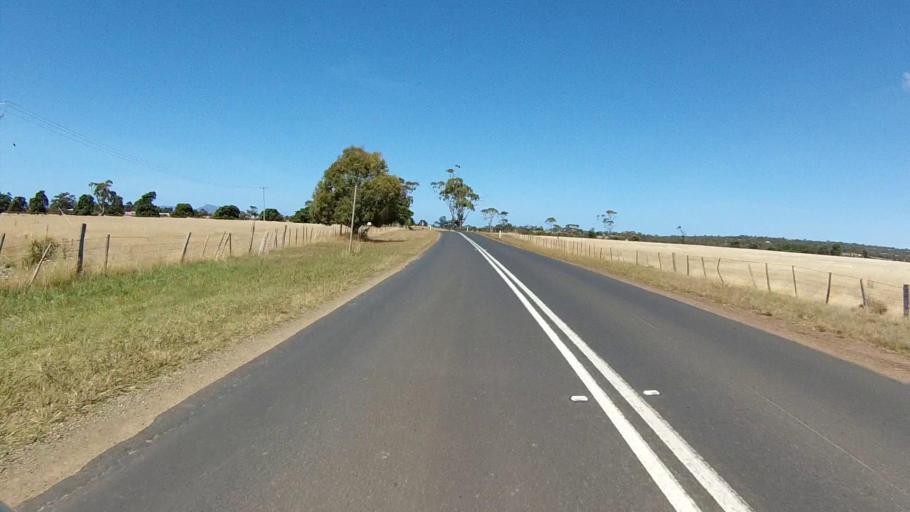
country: AU
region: Tasmania
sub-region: Break O'Day
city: St Helens
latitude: -42.1172
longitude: 148.0621
